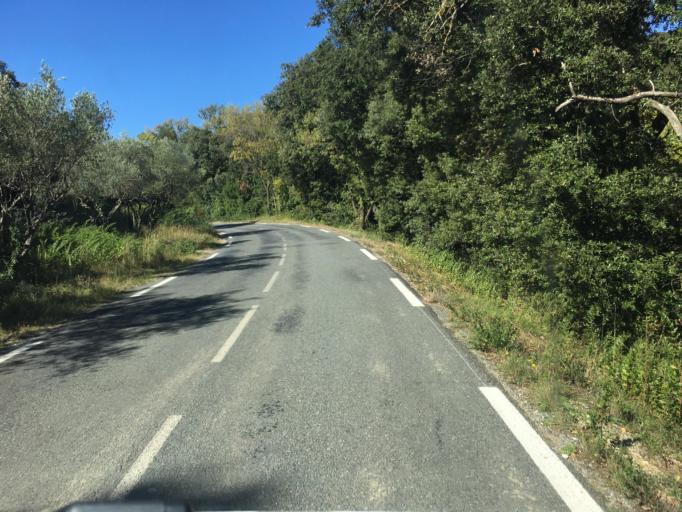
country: FR
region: Languedoc-Roussillon
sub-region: Departement de l'Herault
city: Nebian
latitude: 43.6158
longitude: 3.3737
